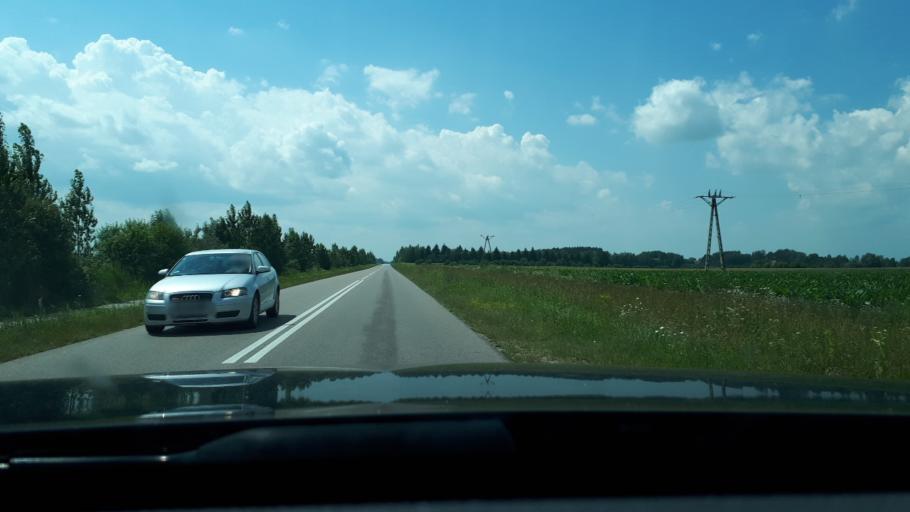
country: PL
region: Podlasie
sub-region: Powiat bialostocki
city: Choroszcz
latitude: 53.1294
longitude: 23.0183
